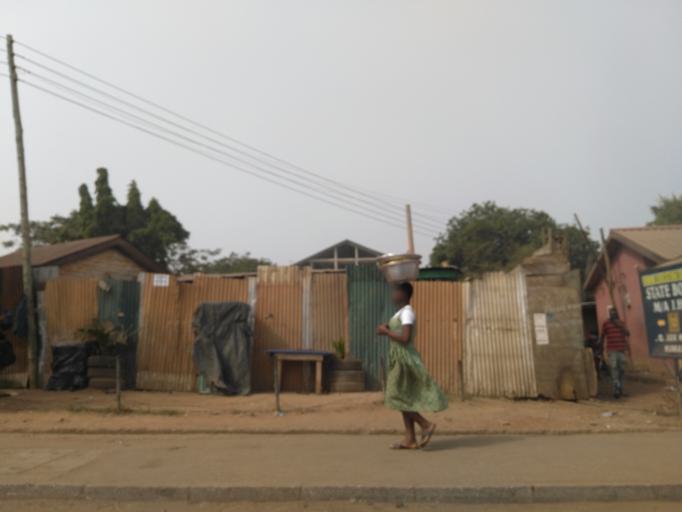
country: GH
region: Ashanti
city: Kumasi
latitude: 6.7095
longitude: -1.6275
